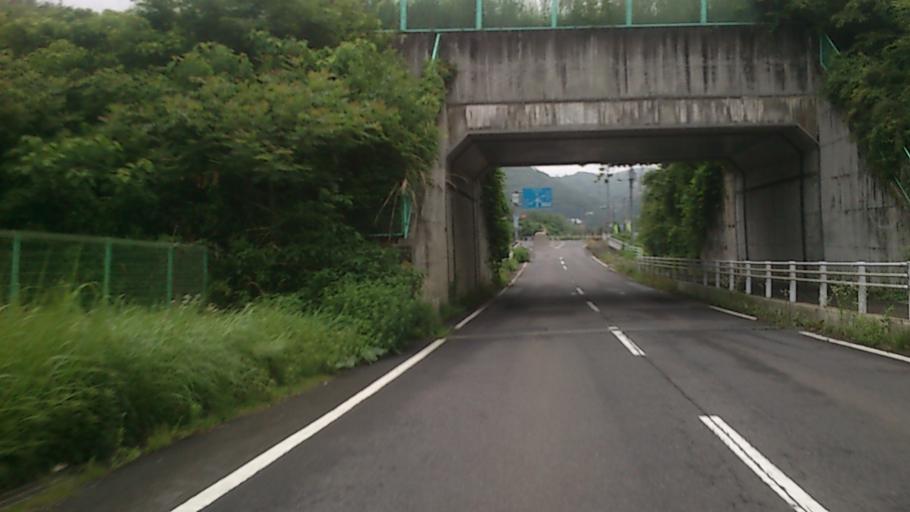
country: JP
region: Ibaraki
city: Omiya
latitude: 36.6325
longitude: 140.3938
